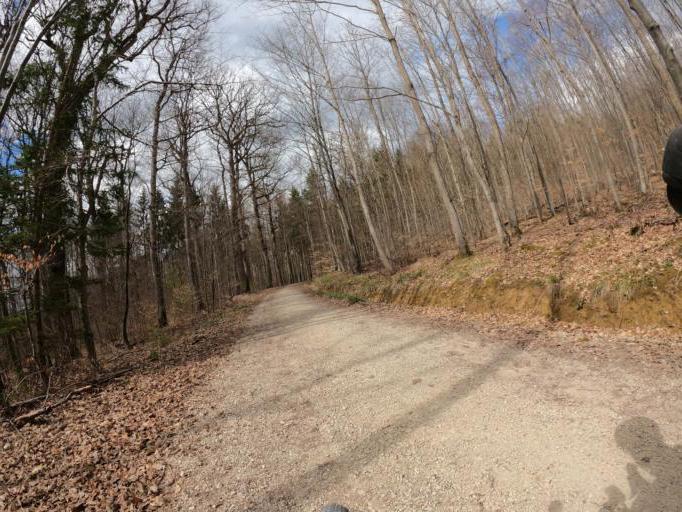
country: DE
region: Baden-Wuerttemberg
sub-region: Tuebingen Region
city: Gomaringen
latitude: 48.4366
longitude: 9.1144
